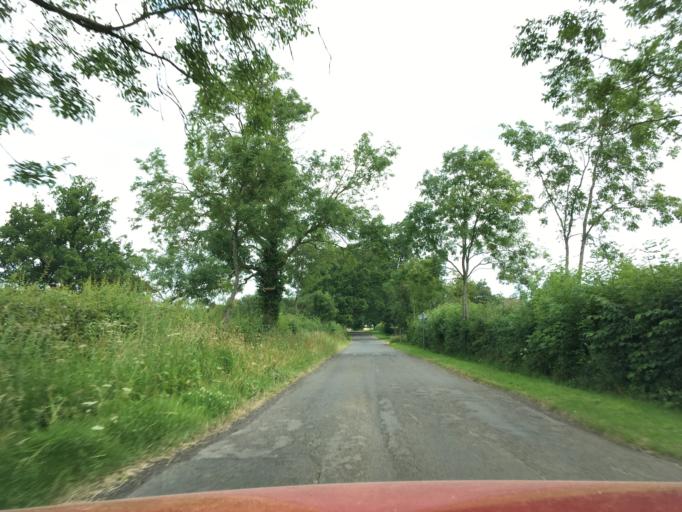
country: GB
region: England
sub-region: Oxfordshire
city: Bloxham
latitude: 51.9582
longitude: -1.3904
